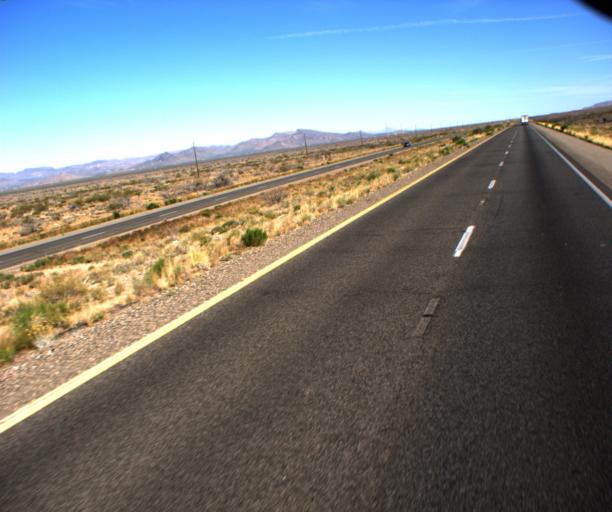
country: US
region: Arizona
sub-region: Mohave County
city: Golden Valley
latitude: 35.2710
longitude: -114.1679
